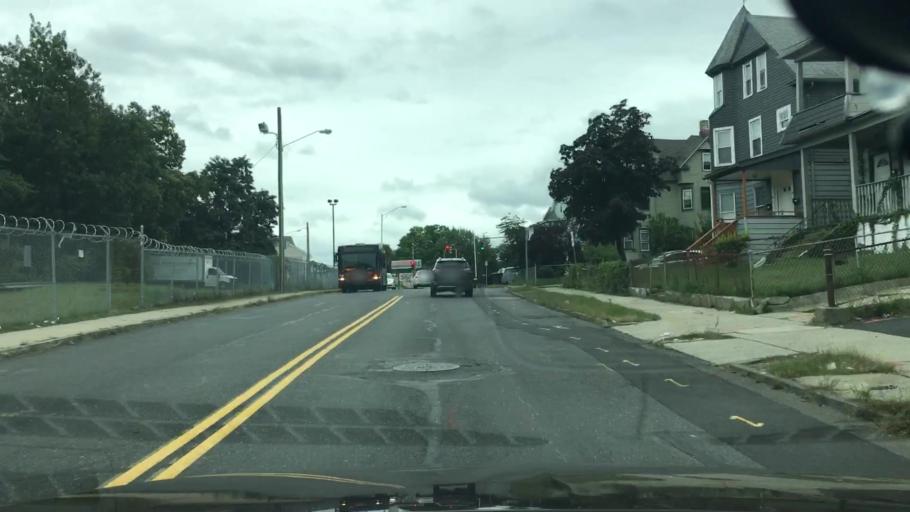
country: US
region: Massachusetts
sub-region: Hampden County
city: Springfield
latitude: 42.0966
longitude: -72.5627
